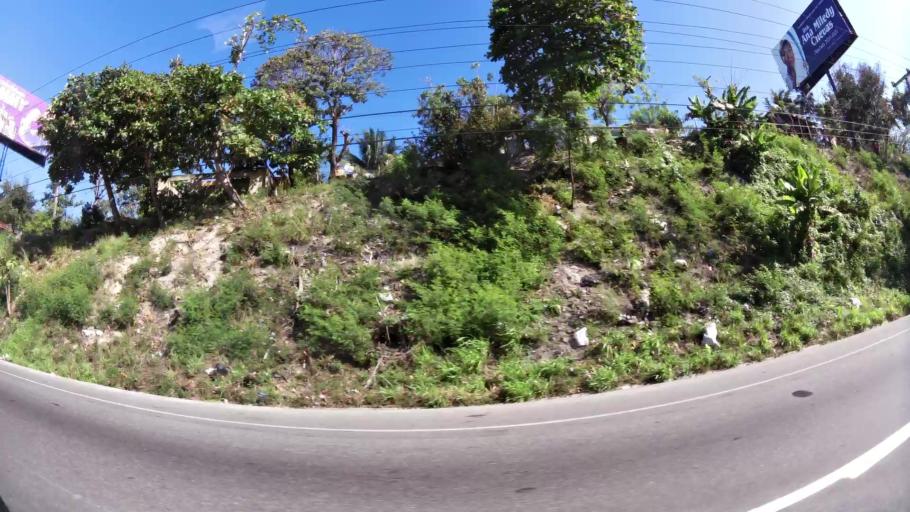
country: DO
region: San Cristobal
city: San Cristobal
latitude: 18.4344
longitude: -70.0796
